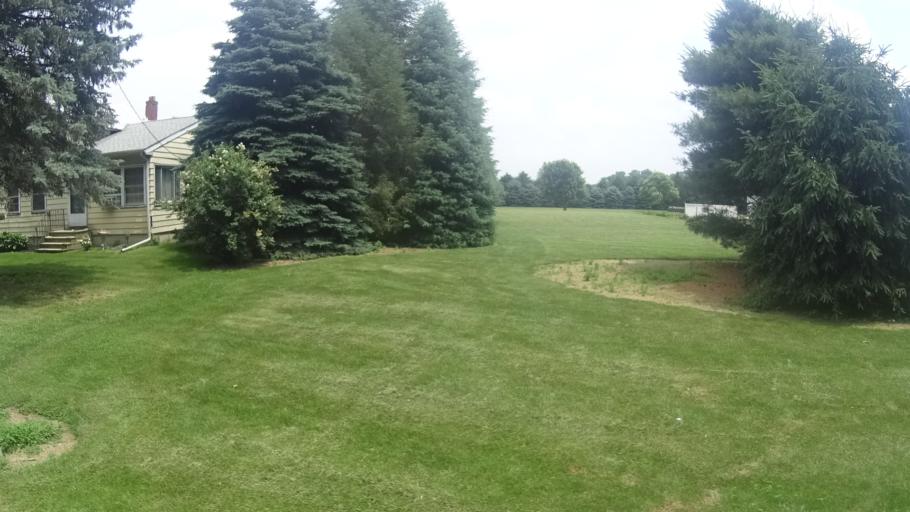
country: US
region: Ohio
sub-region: Erie County
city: Milan
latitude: 41.3018
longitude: -82.6318
